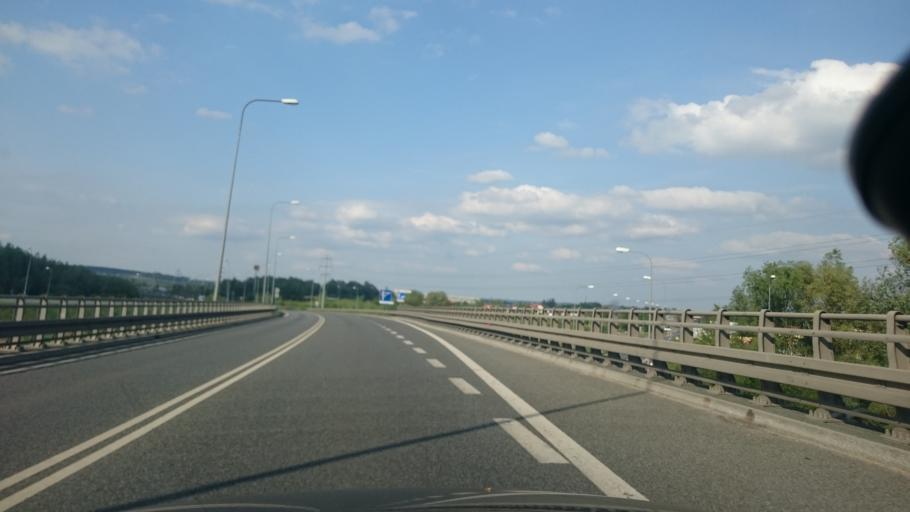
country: PL
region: Kujawsko-Pomorskie
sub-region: Grudziadz
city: Grudziadz
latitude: 53.4829
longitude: 18.7911
